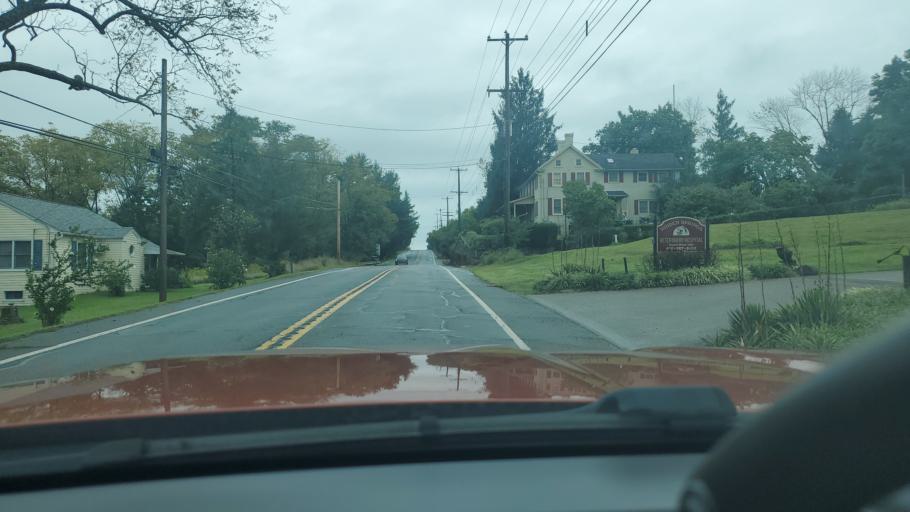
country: US
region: Pennsylvania
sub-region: Montgomery County
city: Spring Mount
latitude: 40.2878
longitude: -75.4814
